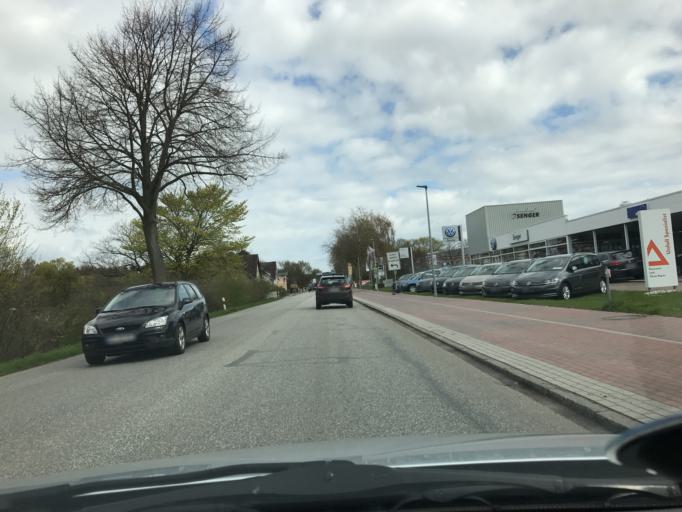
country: DE
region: Schleswig-Holstein
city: Neustadt in Holstein
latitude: 54.1006
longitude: 10.7953
